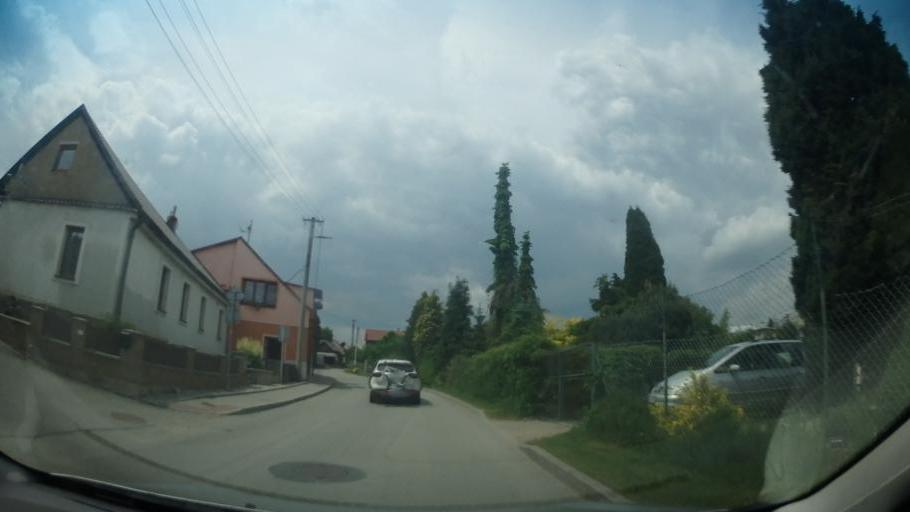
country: CZ
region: South Moravian
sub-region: Okres Blansko
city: Kunstat
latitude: 49.4612
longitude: 16.4650
